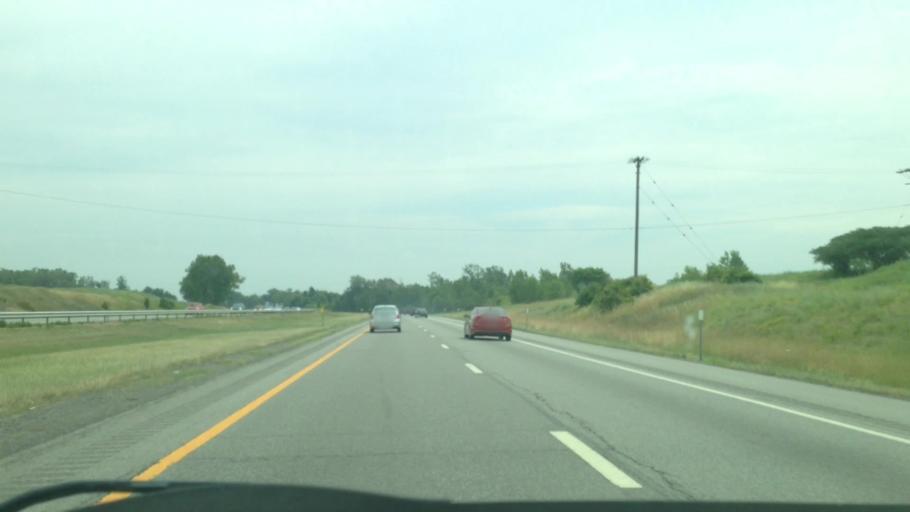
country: US
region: New York
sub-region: Erie County
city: Clarence
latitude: 42.9495
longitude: -78.6125
